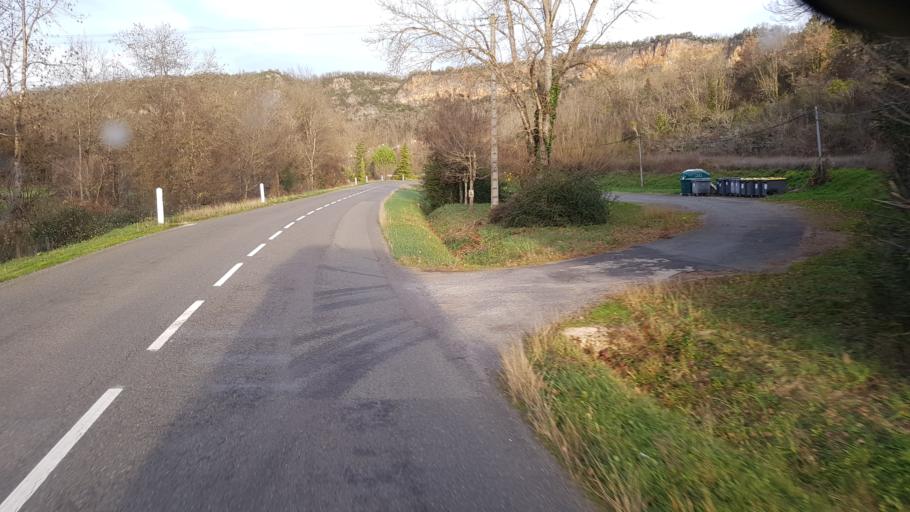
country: FR
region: Midi-Pyrenees
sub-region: Departement du Tarn-et-Garonne
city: Montricoux
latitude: 43.9995
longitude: 1.6947
